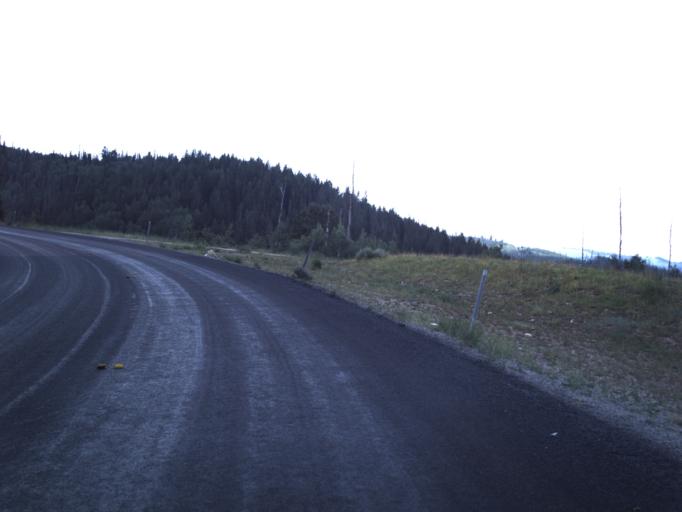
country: US
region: Utah
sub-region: Summit County
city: Francis
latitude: 40.5090
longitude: -111.0460
